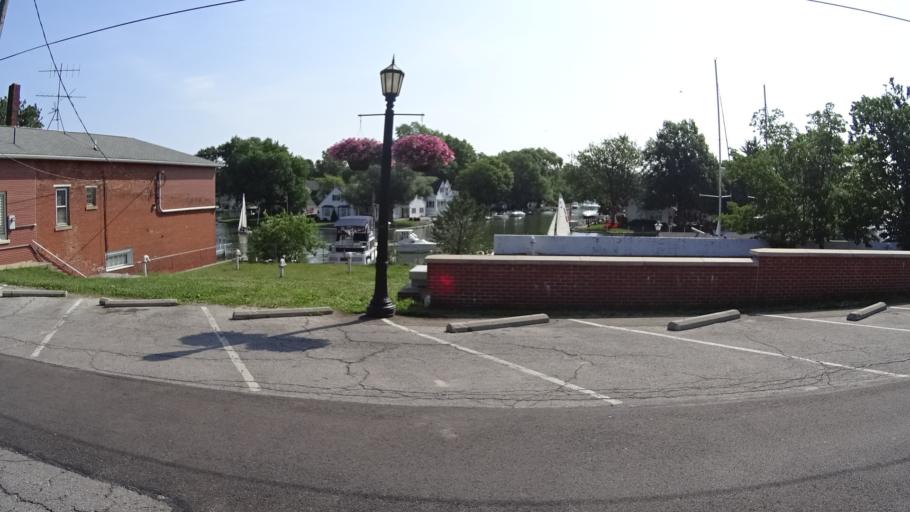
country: US
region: Ohio
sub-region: Lorain County
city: Vermilion
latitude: 41.4236
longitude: -82.3655
